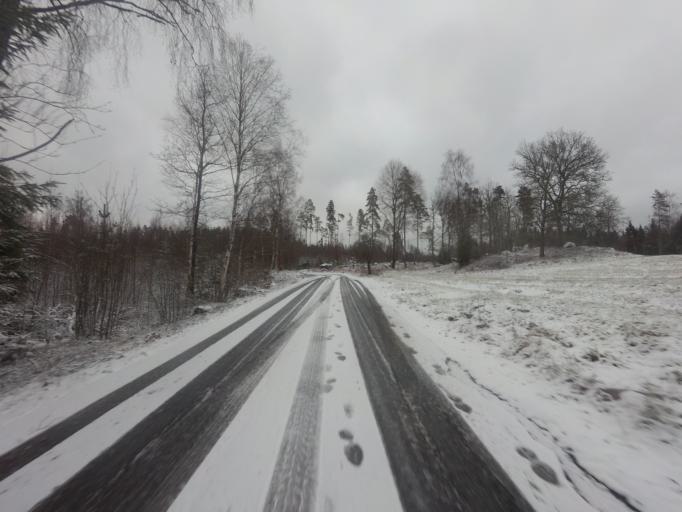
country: SE
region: Skane
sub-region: Osby Kommun
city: Lonsboda
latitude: 56.3947
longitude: 14.2892
